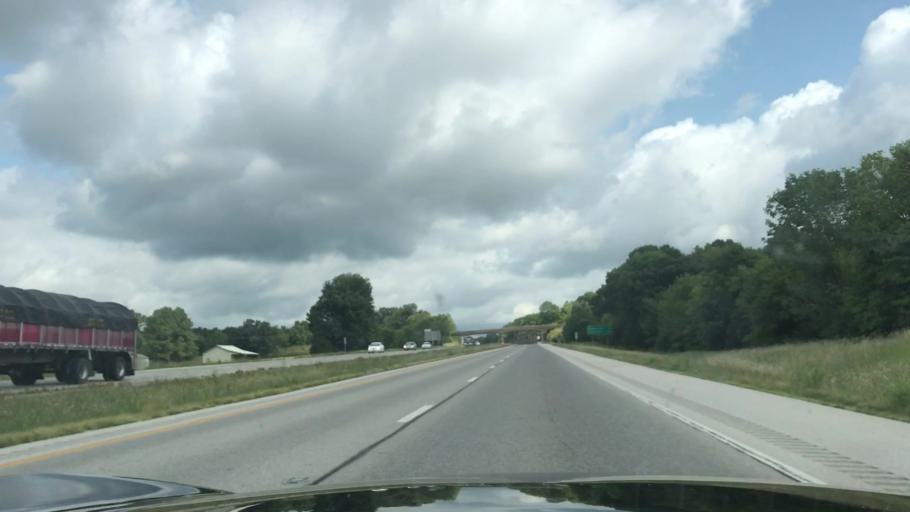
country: US
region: Kentucky
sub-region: Warren County
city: Bowling Green
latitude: 36.9986
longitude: -86.5056
